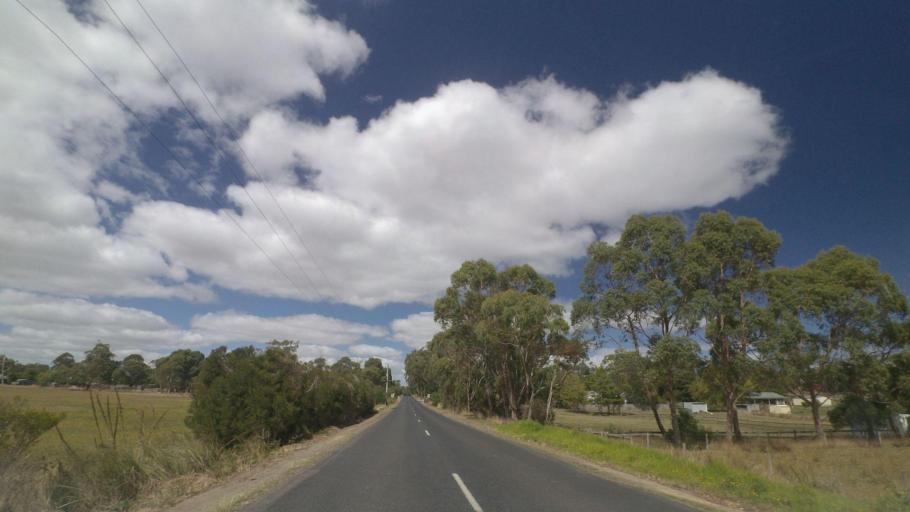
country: AU
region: Victoria
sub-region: Cardinia
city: Koo-Wee-Rup
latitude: -38.3249
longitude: 145.6713
